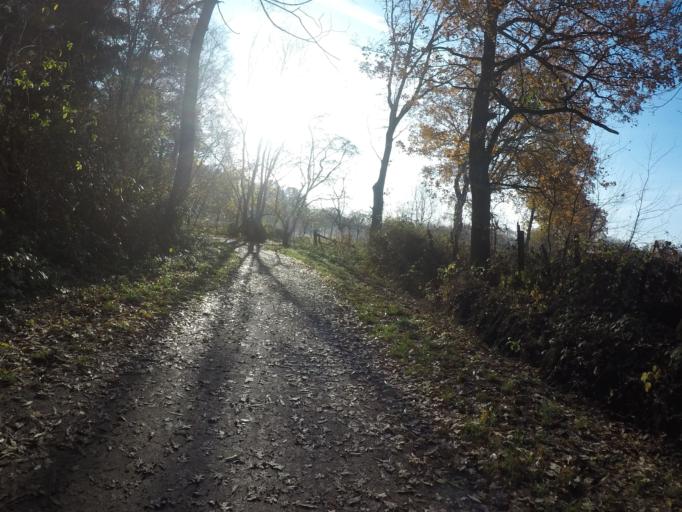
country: DE
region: Hamburg
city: Eidelstedt
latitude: 53.6237
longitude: 9.9240
